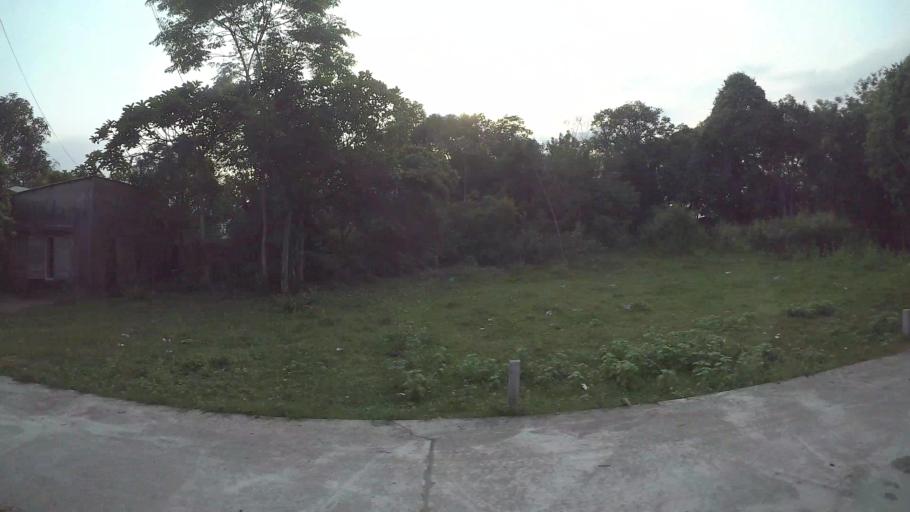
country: VN
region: Da Nang
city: Lien Chieu
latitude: 16.0552
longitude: 108.1071
